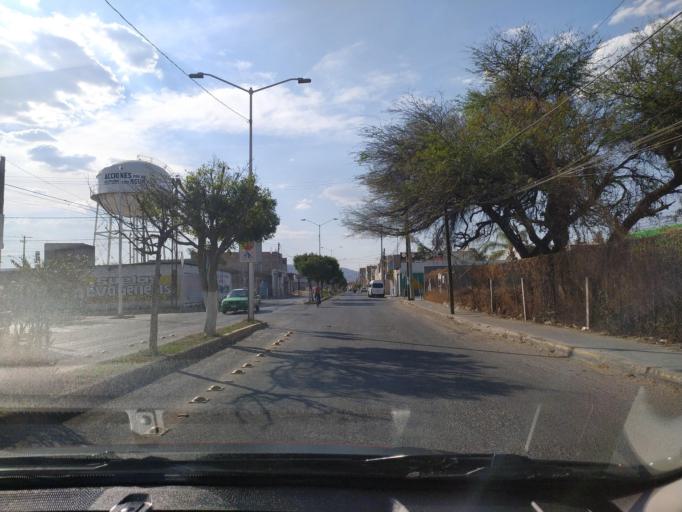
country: MX
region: Guanajuato
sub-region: San Francisco del Rincon
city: Fraccionamiento la Mezquitera
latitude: 21.0130
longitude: -101.8422
